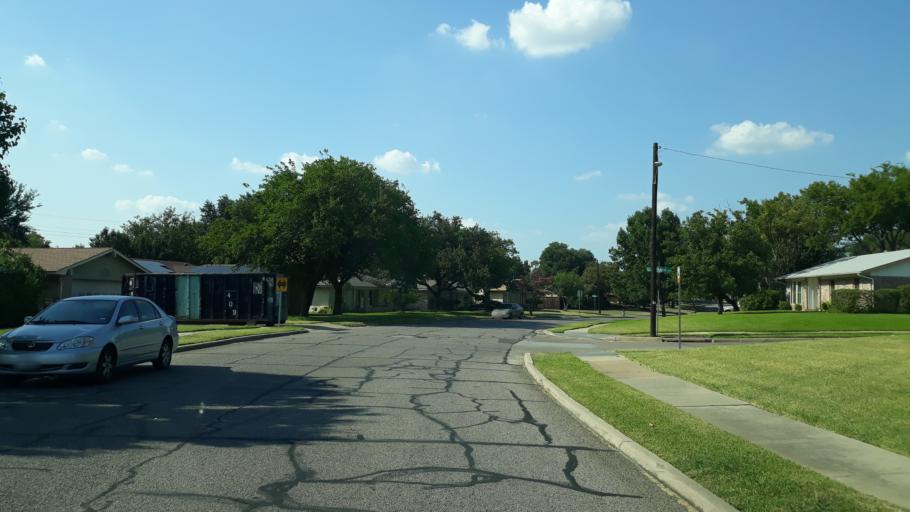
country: US
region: Texas
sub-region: Dallas County
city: Irving
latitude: 32.8432
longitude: -96.9986
